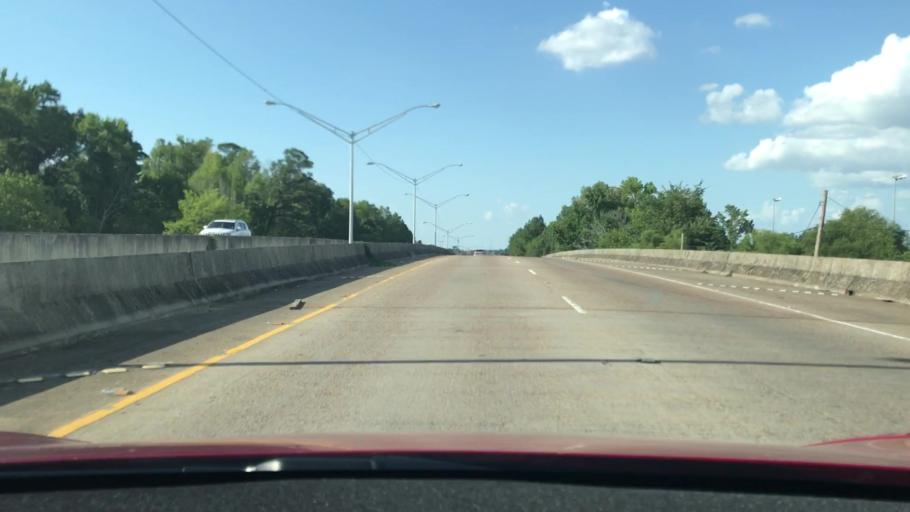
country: US
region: Louisiana
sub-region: Bossier Parish
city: Bossier City
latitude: 32.4298
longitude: -93.7847
